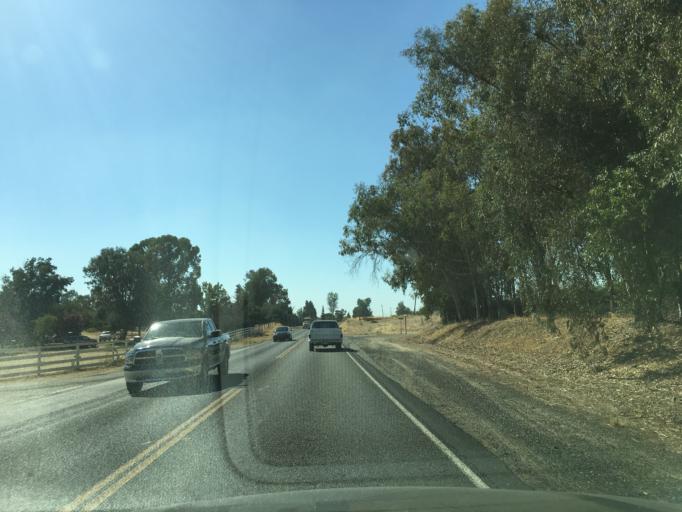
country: US
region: California
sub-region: Madera County
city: Parksdale
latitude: 36.9966
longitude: -119.9865
